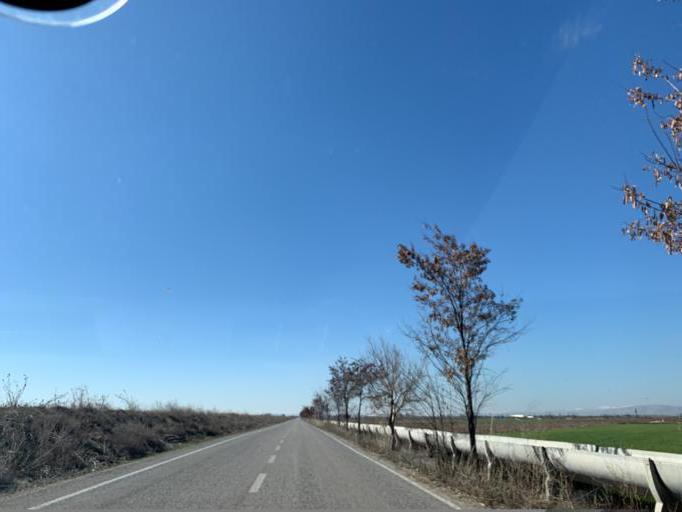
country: TR
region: Konya
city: Catalhoeyuek
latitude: 37.6261
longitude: 32.8060
